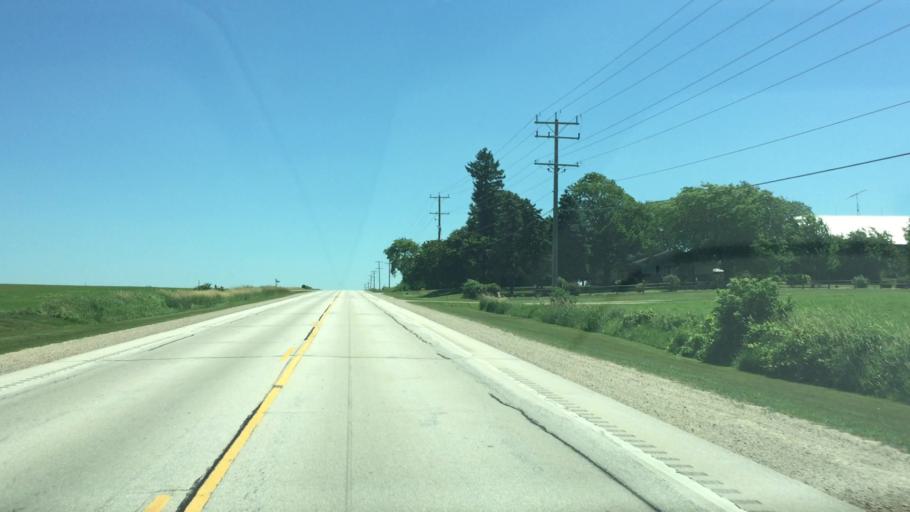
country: US
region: Wisconsin
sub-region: Calumet County
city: Sherwood
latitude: 44.1407
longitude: -88.2373
